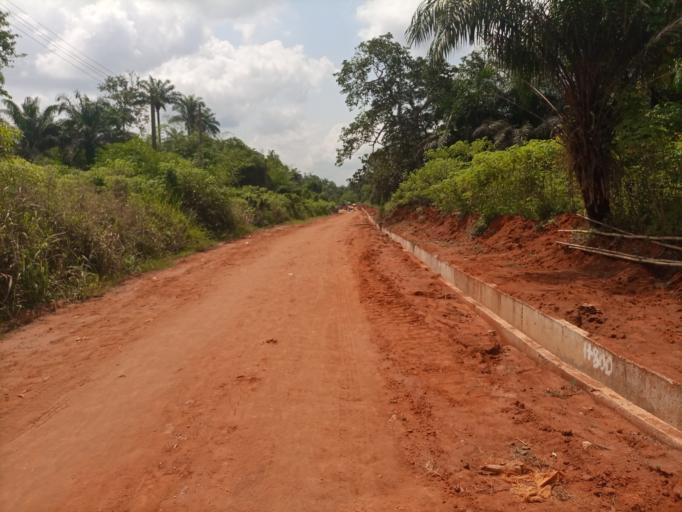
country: NG
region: Abia
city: Umuahia
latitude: 5.4808
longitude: 7.3300
